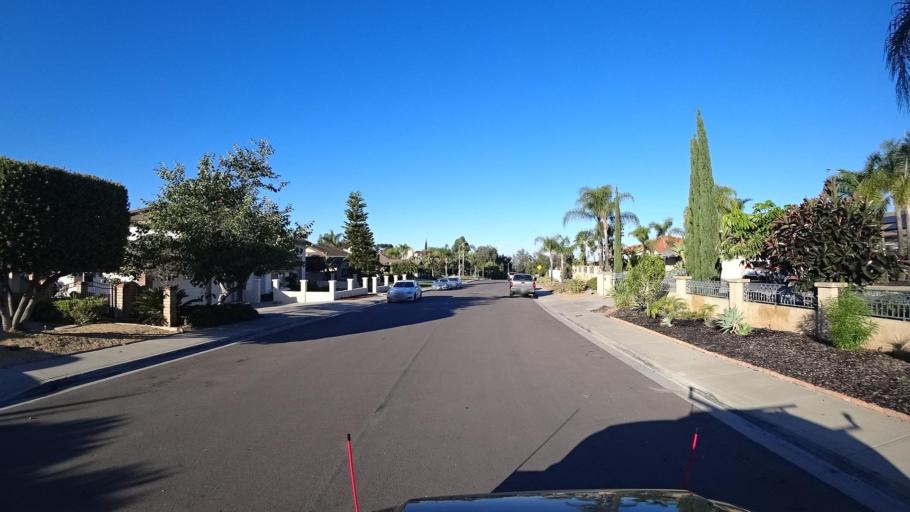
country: US
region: California
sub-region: San Diego County
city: Bonita
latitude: 32.6681
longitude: -117.0424
